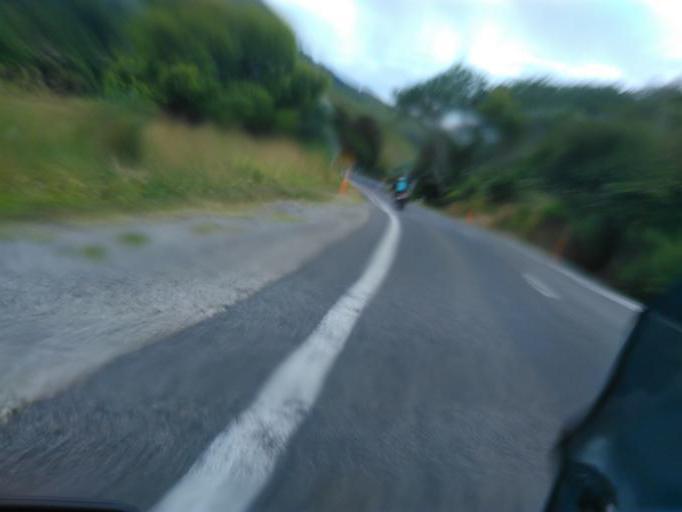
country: NZ
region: Gisborne
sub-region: Gisborne District
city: Gisborne
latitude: -38.4567
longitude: 177.6404
